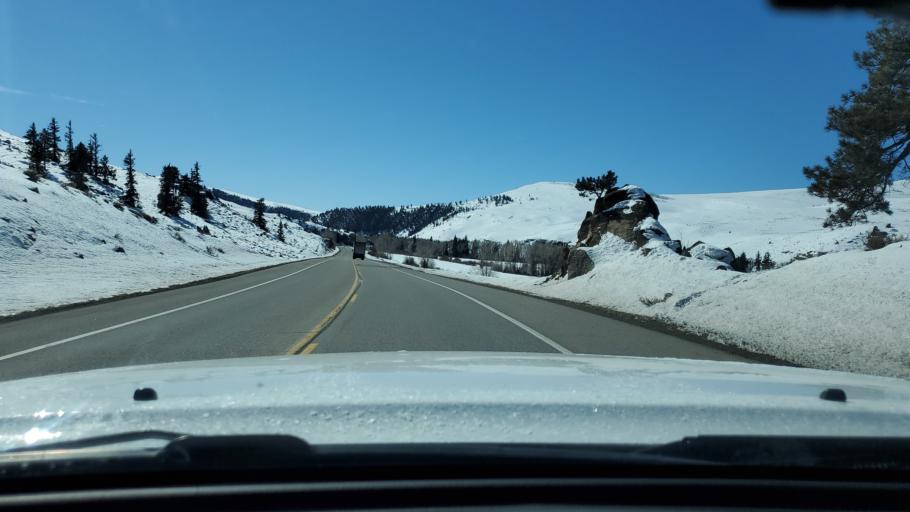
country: US
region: Colorado
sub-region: Gunnison County
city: Gunnison
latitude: 38.6914
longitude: -106.8524
